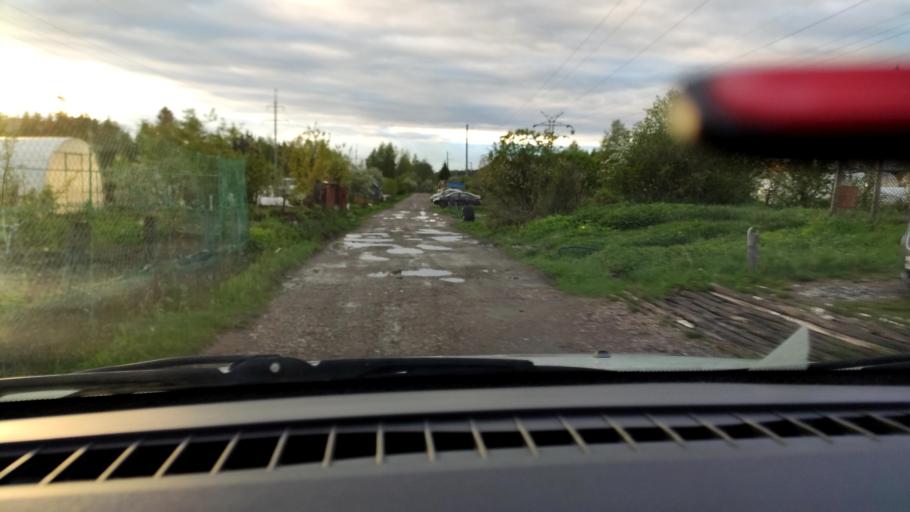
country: RU
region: Perm
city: Polazna
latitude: 58.1316
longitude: 56.4127
